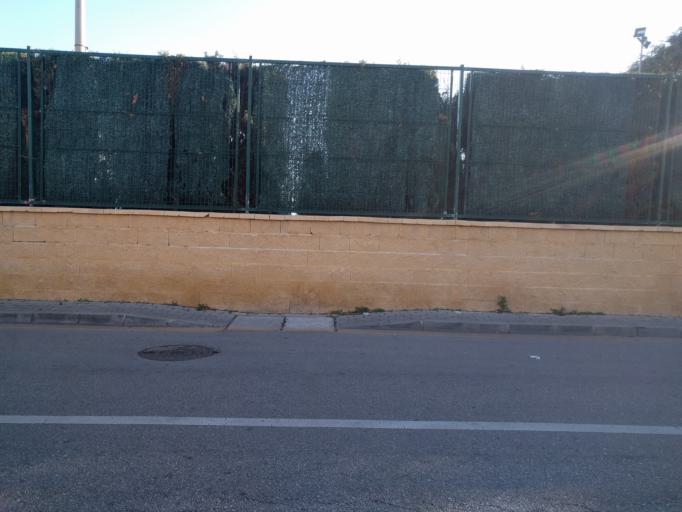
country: ES
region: Andalusia
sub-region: Provincia de Malaga
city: Torremolinos
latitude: 36.6705
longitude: -4.4826
